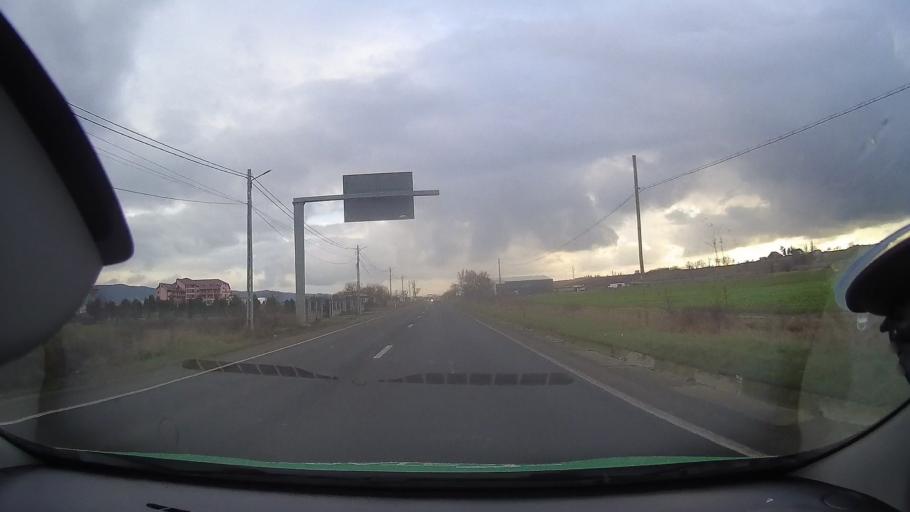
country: RO
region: Cluj
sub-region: Comuna Viisoara
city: Viisoara
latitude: 46.5206
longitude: 23.9102
